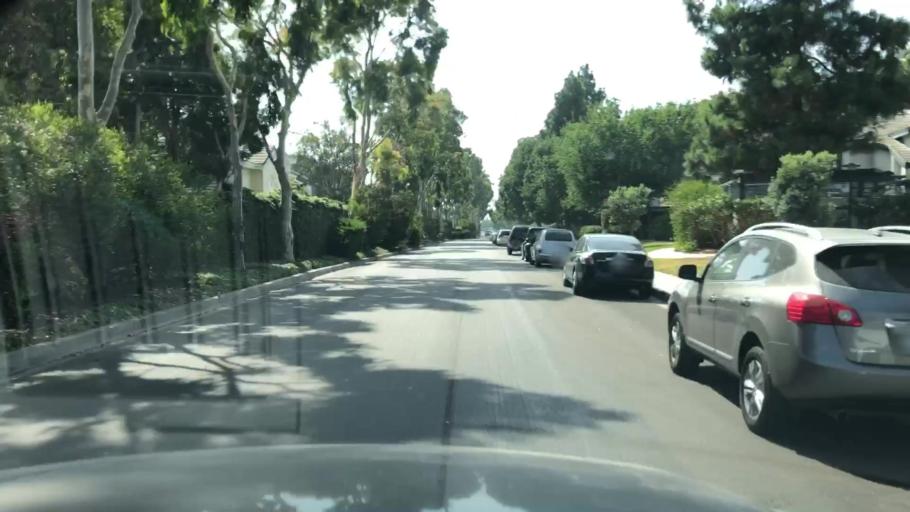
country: US
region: California
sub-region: Ventura County
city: Channel Islands Beach
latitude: 34.1786
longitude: -119.2131
